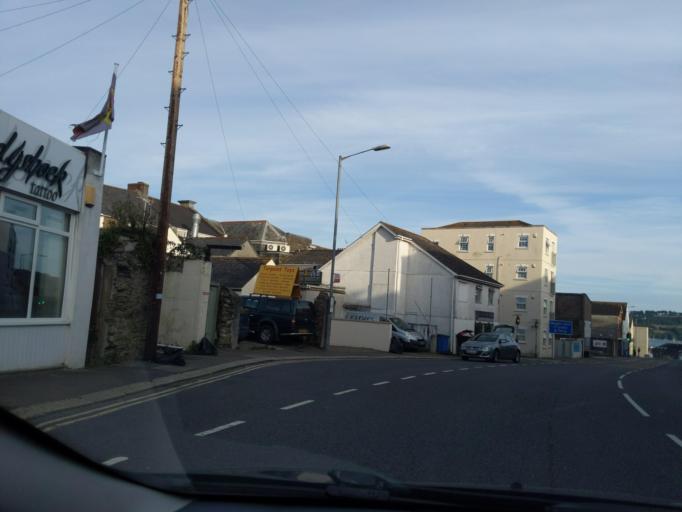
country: GB
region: England
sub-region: Cornwall
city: Torpoint
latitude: 50.3760
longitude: -4.1963
